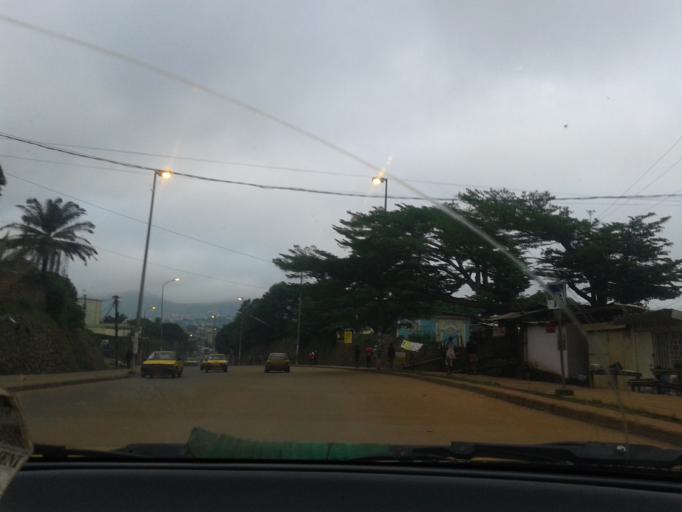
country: CM
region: Centre
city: Yaounde
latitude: 3.8830
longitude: 11.5221
